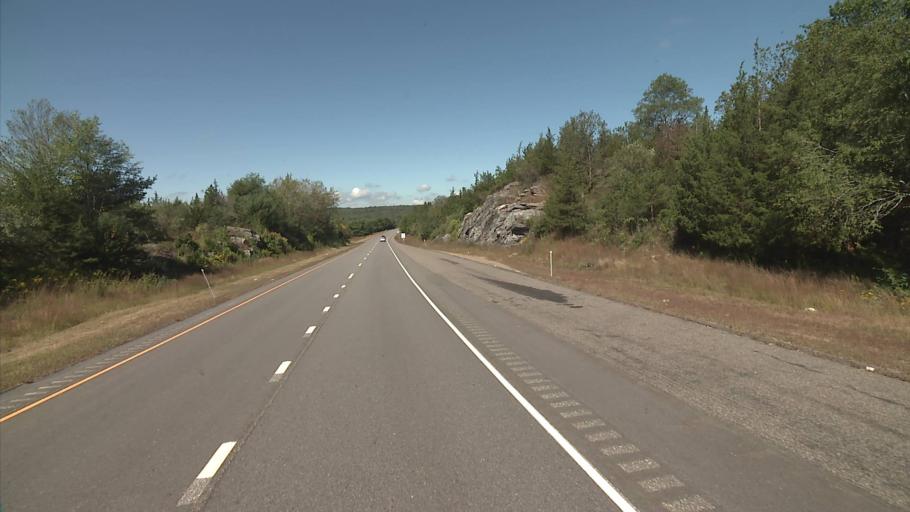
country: US
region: Connecticut
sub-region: New London County
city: Colchester
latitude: 41.4676
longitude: -72.2825
